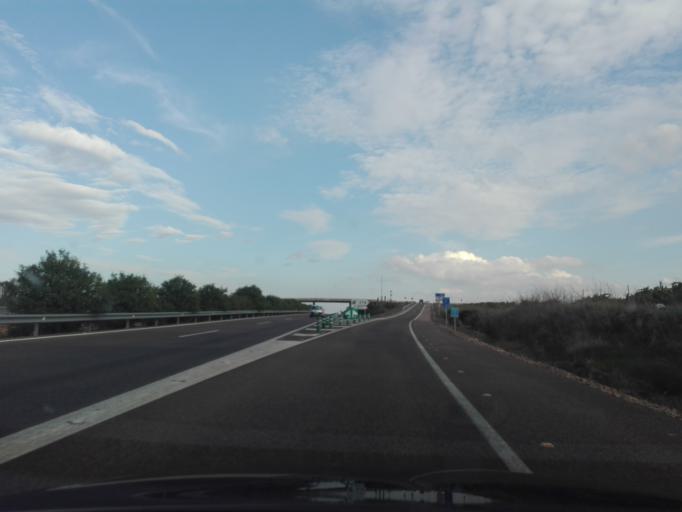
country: ES
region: Extremadura
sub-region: Provincia de Badajoz
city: Valdelacalzada
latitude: 38.8510
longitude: -6.7164
